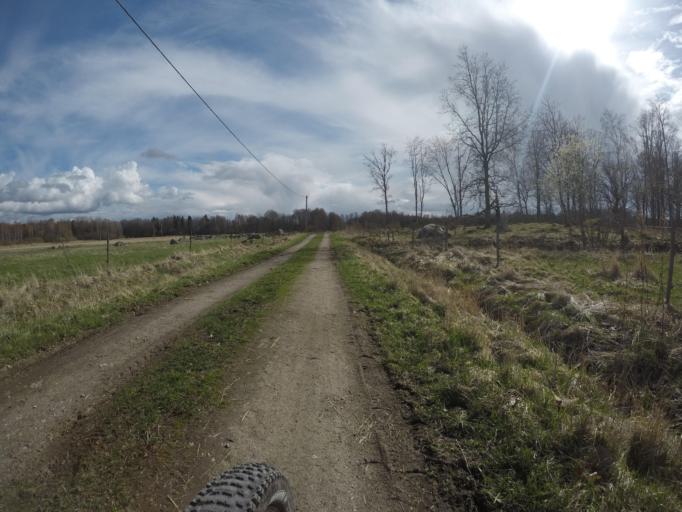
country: SE
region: Vaestmanland
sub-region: Kungsors Kommun
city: Kungsoer
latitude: 59.2747
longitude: 16.1525
